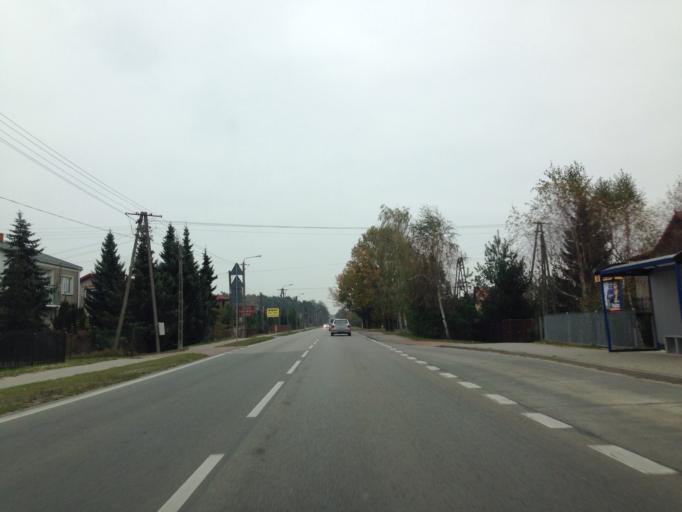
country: PL
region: Masovian Voivodeship
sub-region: Powiat warszawski zachodni
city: Leszno
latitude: 52.2619
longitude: 20.6297
